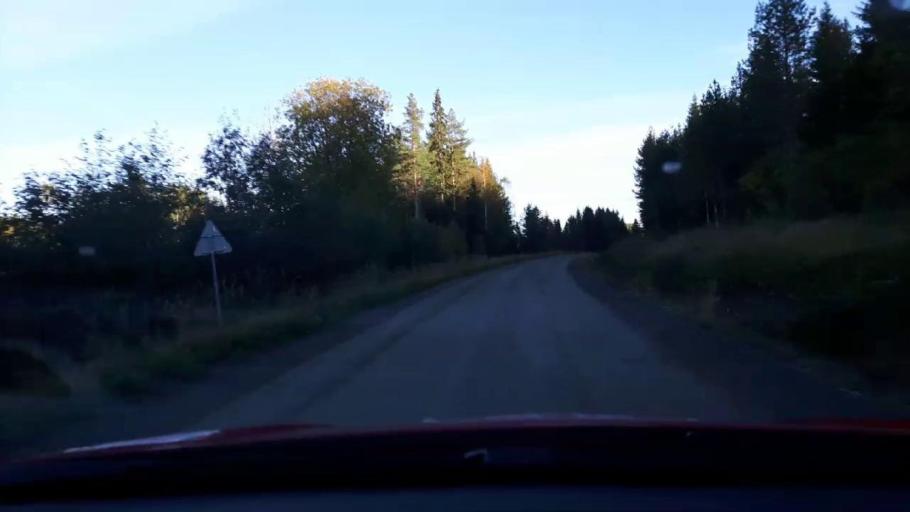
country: SE
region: Jaemtland
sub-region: OEstersunds Kommun
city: Brunflo
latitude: 62.9443
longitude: 14.9853
